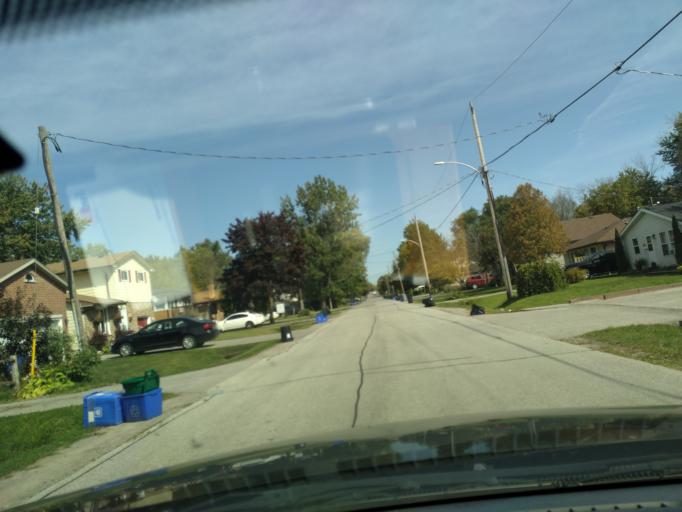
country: CA
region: Ontario
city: Keswick
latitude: 44.2028
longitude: -79.4764
